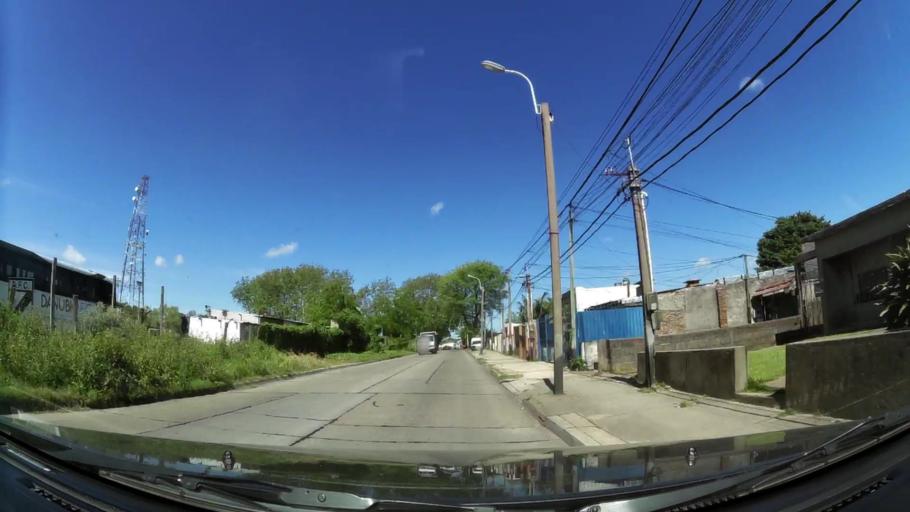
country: UY
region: Montevideo
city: Montevideo
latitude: -34.8475
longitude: -56.1316
